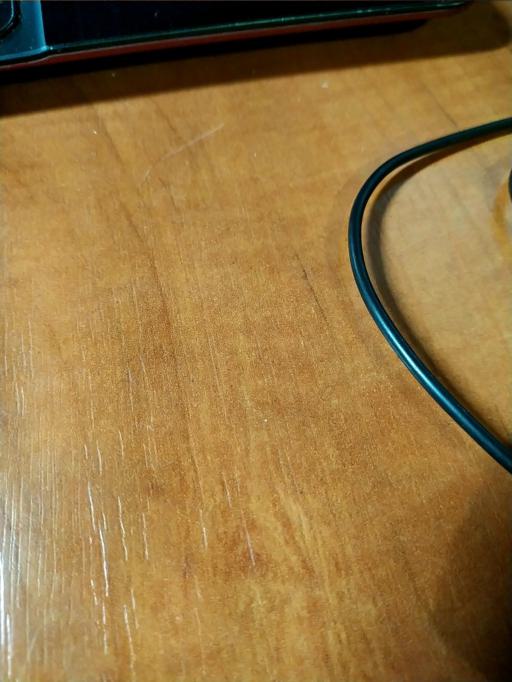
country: RU
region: Smolensk
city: Yartsevo
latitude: 55.4130
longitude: 32.8343
